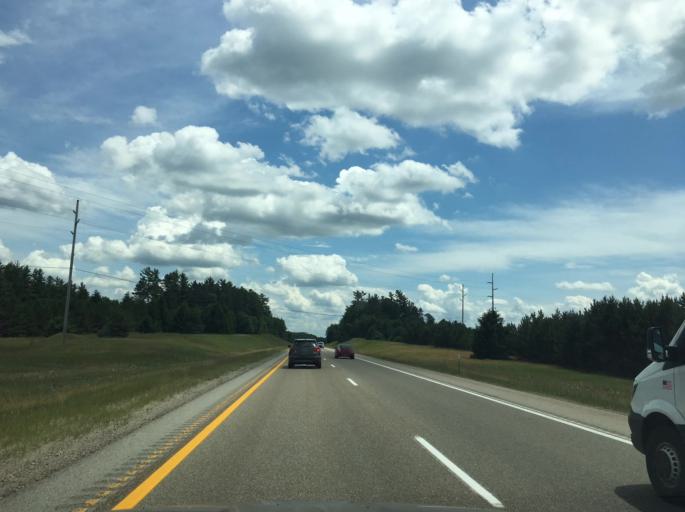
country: US
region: Michigan
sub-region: Roscommon County
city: Roscommon
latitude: 44.5392
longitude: -84.6910
